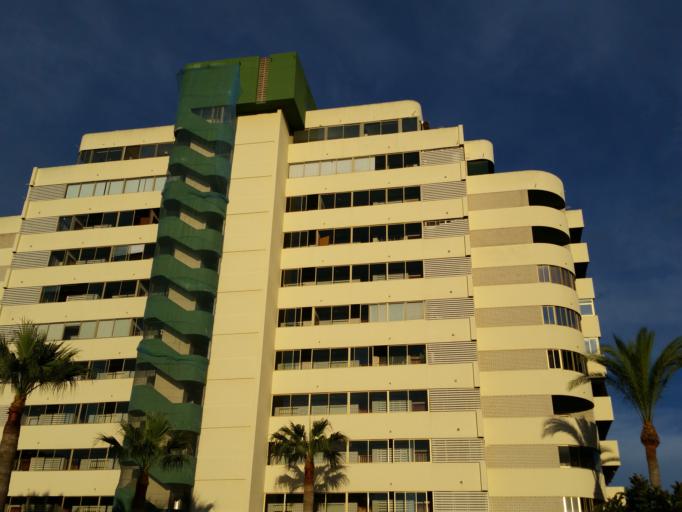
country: ES
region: Andalusia
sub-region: Provincia de Malaga
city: Fuengirola
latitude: 36.5588
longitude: -4.6099
